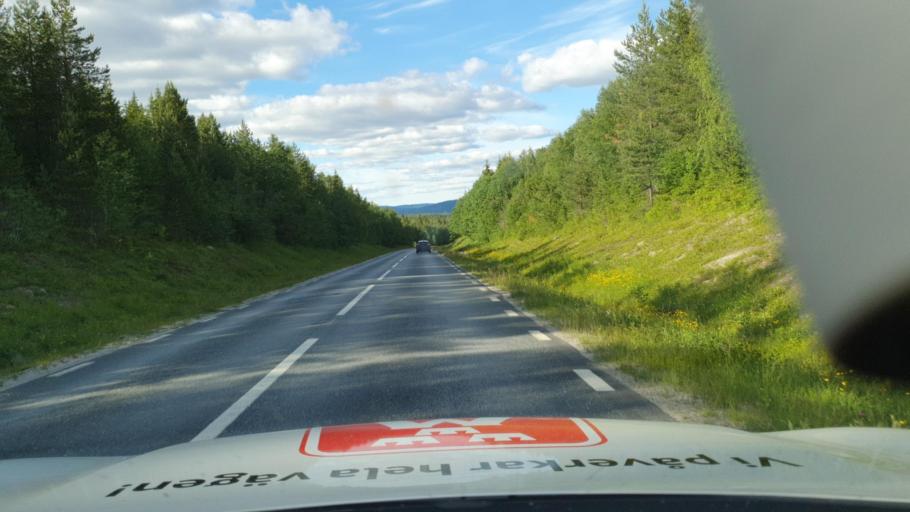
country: SE
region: Vaesterbotten
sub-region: Lycksele Kommun
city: Lycksele
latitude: 64.4957
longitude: 18.2918
